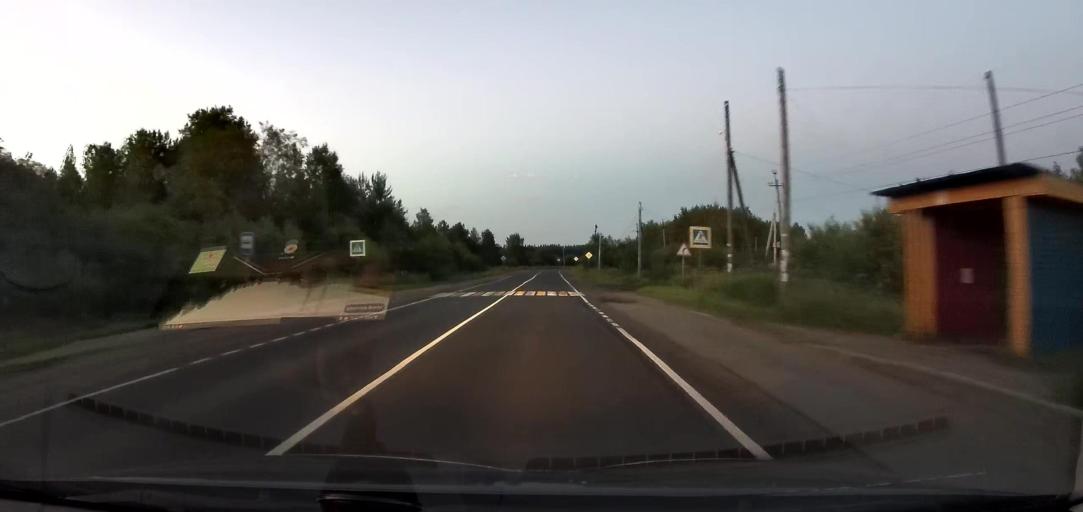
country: RU
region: Arkhangelskaya
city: Uyemskiy
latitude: 64.4413
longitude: 40.9580
